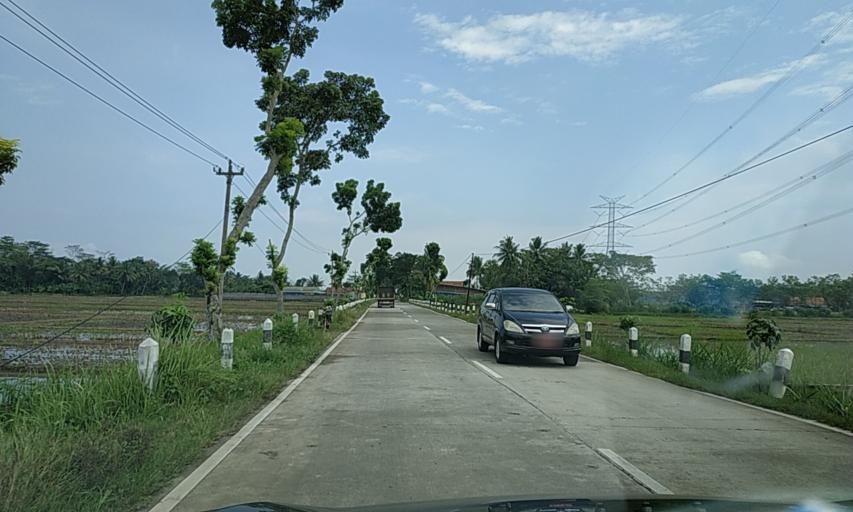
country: ID
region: Central Java
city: Tambangan
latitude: -7.4828
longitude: 108.8278
